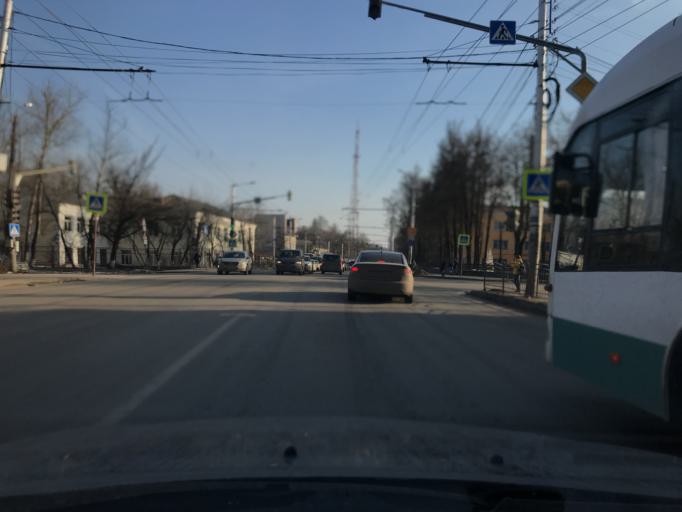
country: RU
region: Kaluga
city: Kaluga
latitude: 54.5278
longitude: 36.2614
